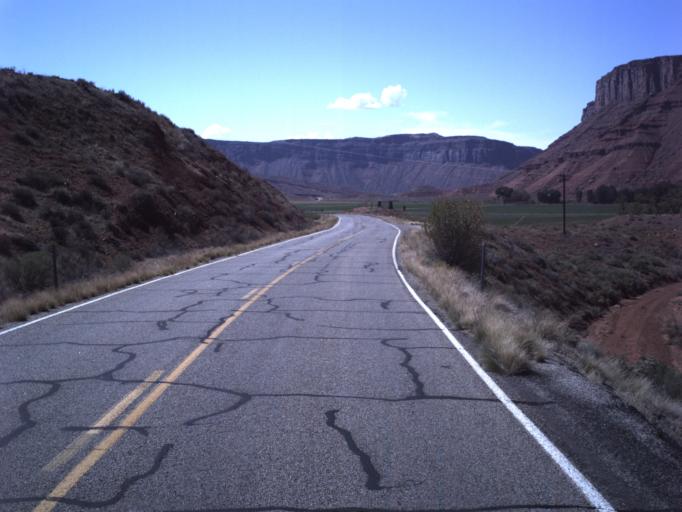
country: US
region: Utah
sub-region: Grand County
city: Moab
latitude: 38.7023
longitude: -109.3917
